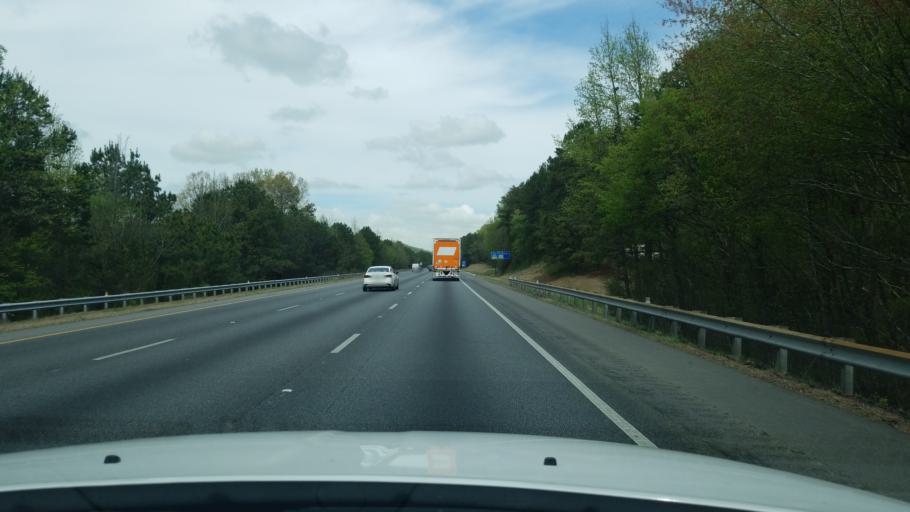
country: US
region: Georgia
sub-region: Whitfield County
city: Varnell
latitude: 34.8418
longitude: -85.0172
